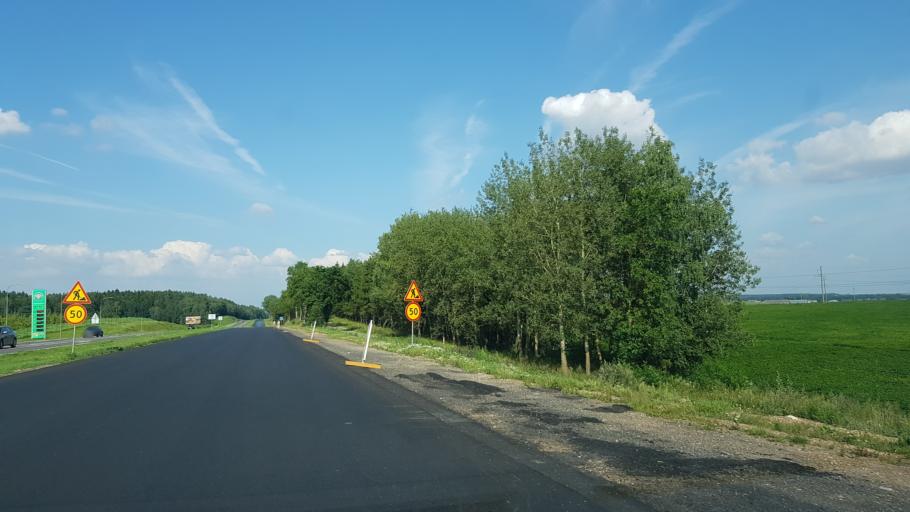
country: BY
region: Minsk
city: Dzyarzhynsk
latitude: 53.6934
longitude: 27.1737
